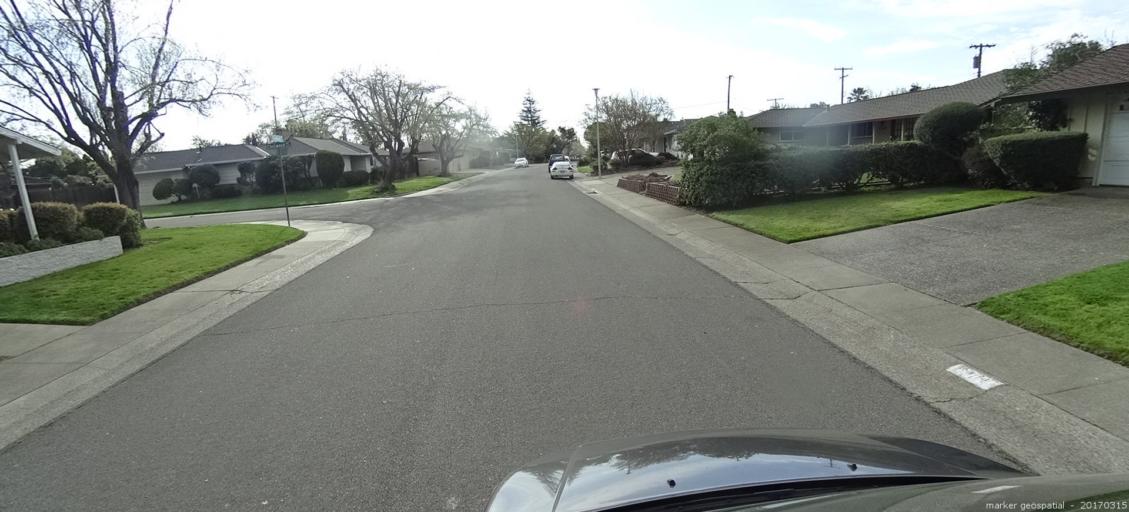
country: US
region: California
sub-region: Sacramento County
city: Parkway
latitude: 38.5075
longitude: -121.5106
